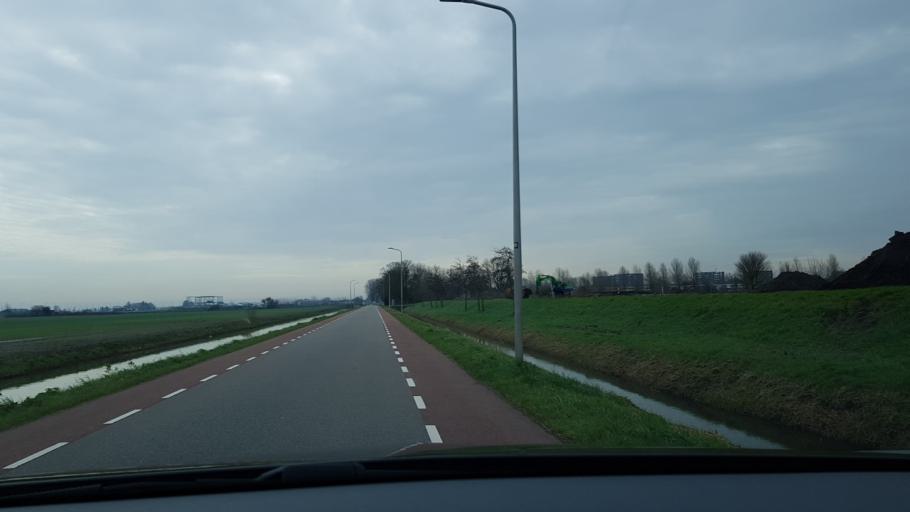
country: NL
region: North Holland
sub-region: Gemeente Uithoorn
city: Uithoorn
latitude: 52.2569
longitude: 4.8096
